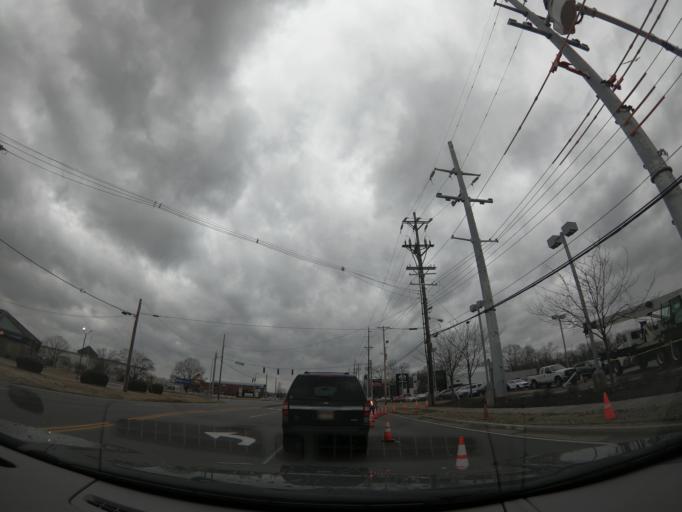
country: US
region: Kentucky
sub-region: Jefferson County
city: Lyndon
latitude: 38.2489
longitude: -85.6058
